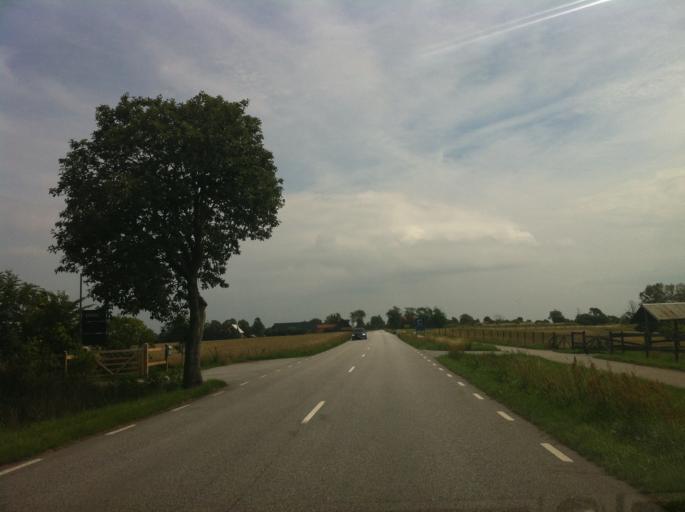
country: SE
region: Skane
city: Smygehamn
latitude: 55.3441
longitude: 13.3157
